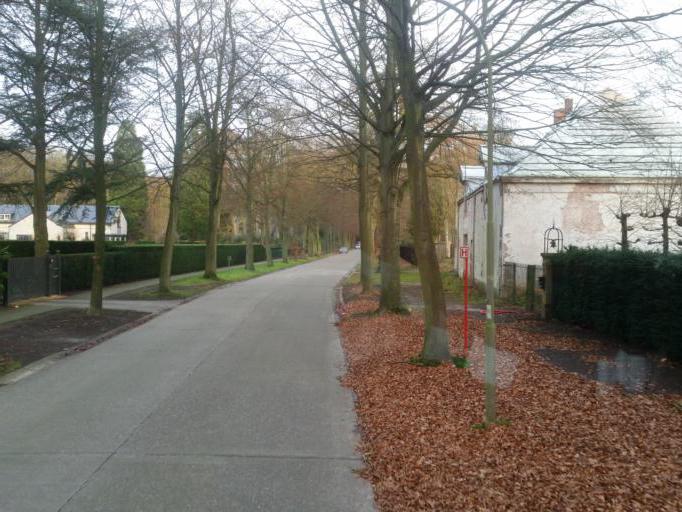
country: BE
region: Flanders
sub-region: Provincie Antwerpen
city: Brasschaat
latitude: 51.3216
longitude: 4.4904
